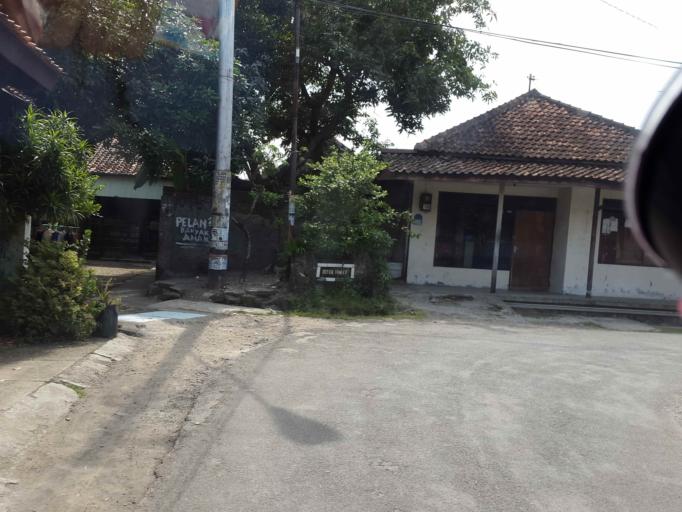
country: ID
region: Central Java
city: Pemalang
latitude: -6.8959
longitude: 109.3846
